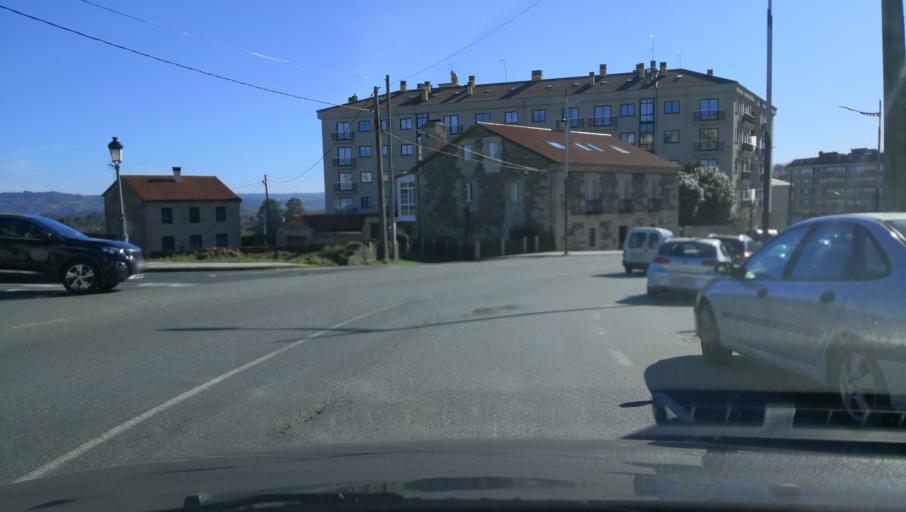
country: ES
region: Galicia
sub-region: Provincia de Pontevedra
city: Silleda
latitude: 42.6972
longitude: -8.2445
